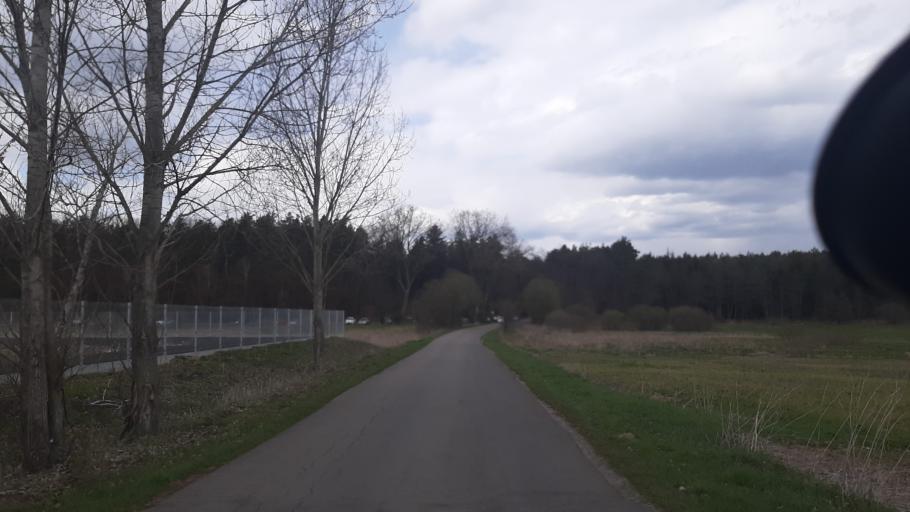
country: PL
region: Lublin Voivodeship
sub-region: Powiat lubelski
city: Niemce
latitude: 51.3669
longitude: 22.5526
